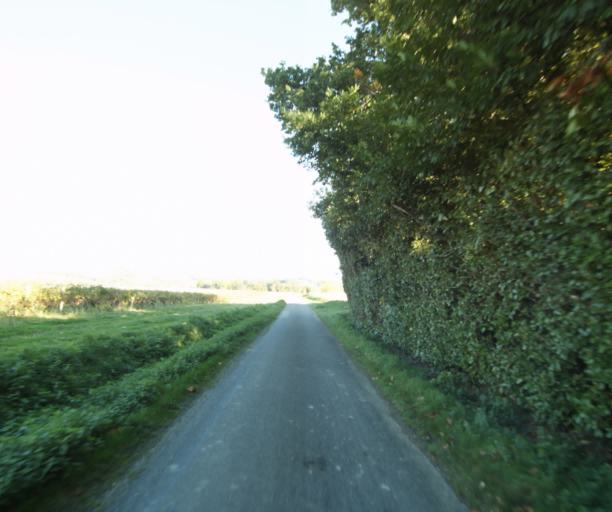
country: FR
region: Midi-Pyrenees
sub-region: Departement du Gers
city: Eauze
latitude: 43.7722
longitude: 0.1541
